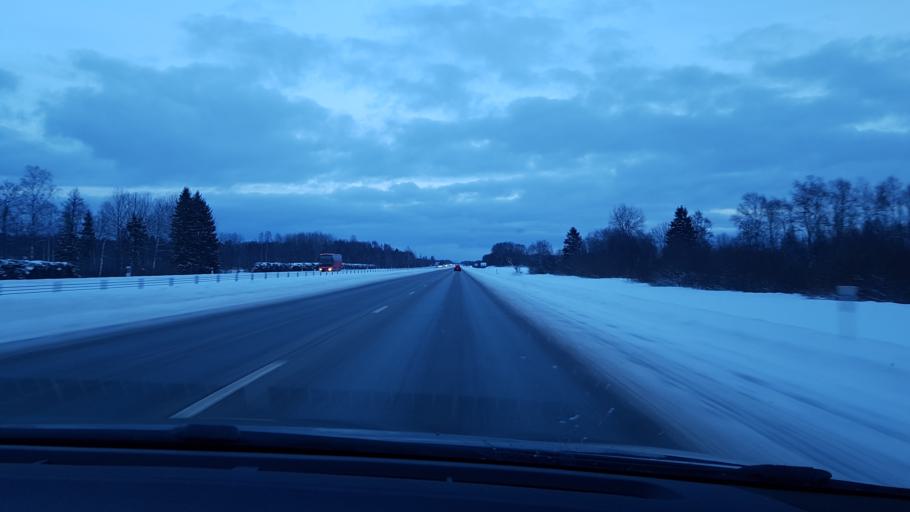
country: EE
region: Harju
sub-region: Anija vald
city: Kehra
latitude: 59.4427
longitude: 25.3317
